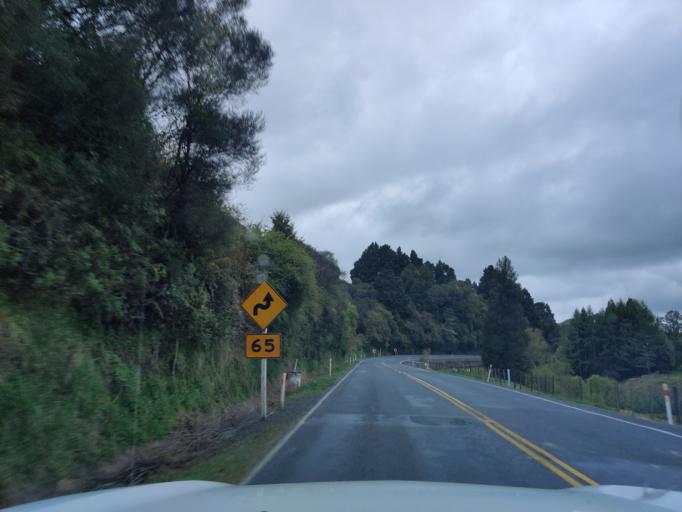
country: NZ
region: Waikato
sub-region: Otorohanga District
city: Otorohanga
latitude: -38.6104
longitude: 175.2174
